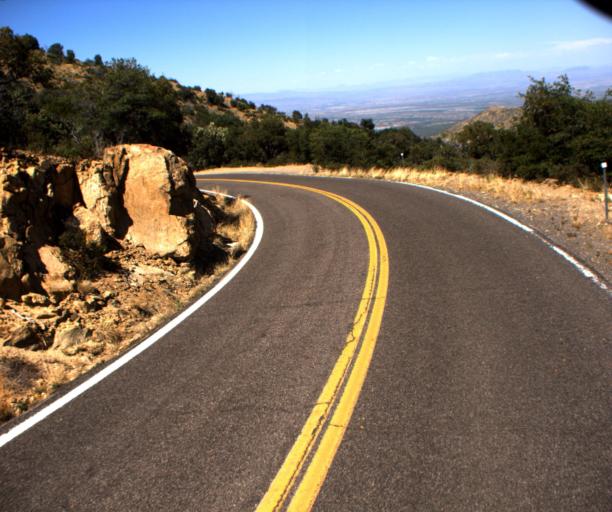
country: US
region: Arizona
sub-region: Graham County
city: Swift Trail Junction
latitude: 32.6588
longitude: -109.8037
